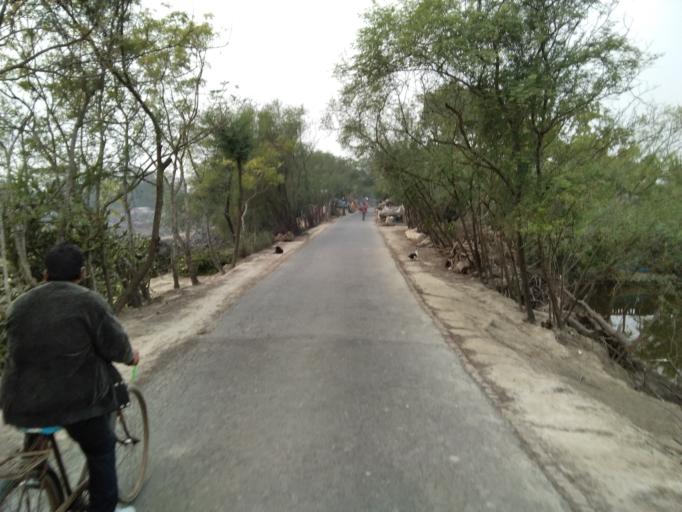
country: BD
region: Khulna
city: Satkhira
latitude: 22.5816
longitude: 89.0680
